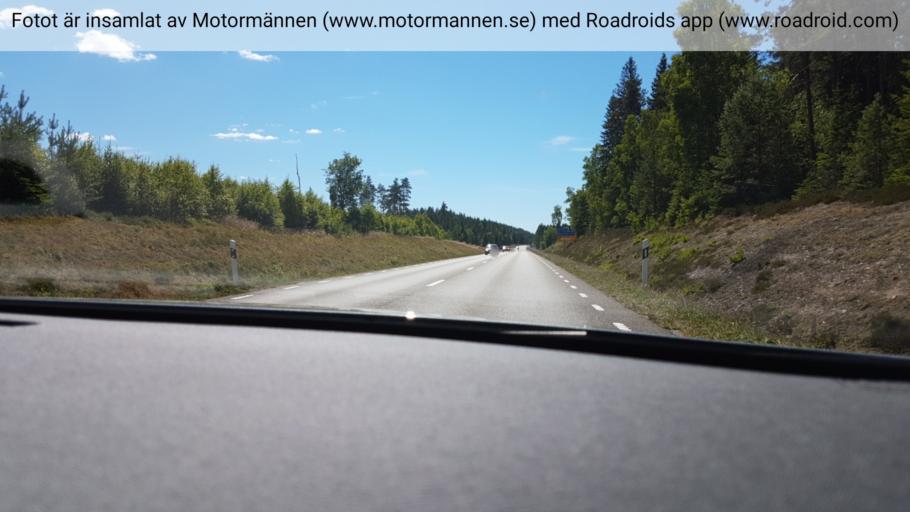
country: SE
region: Joenkoeping
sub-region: Gnosjo Kommun
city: Marieholm
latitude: 57.6177
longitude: 13.7691
